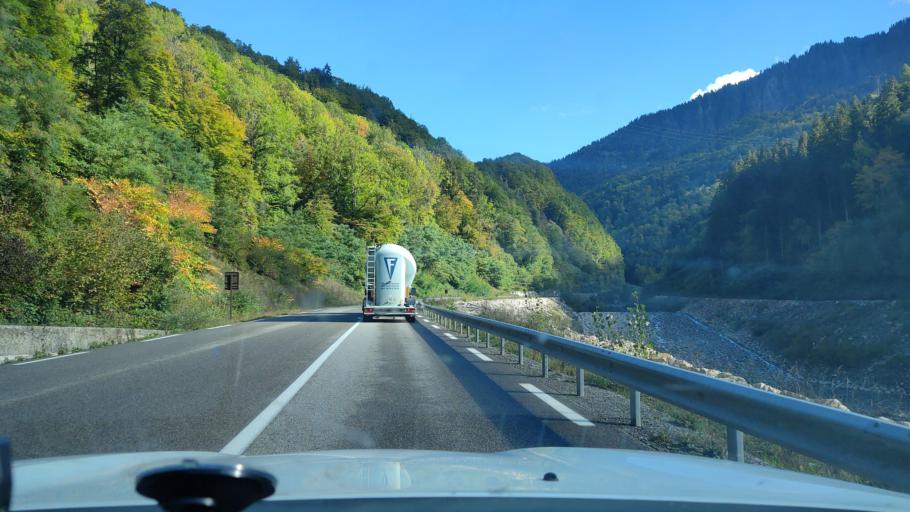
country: FR
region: Rhone-Alpes
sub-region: Departement de la Savoie
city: Ugine
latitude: 45.7611
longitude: 6.4732
